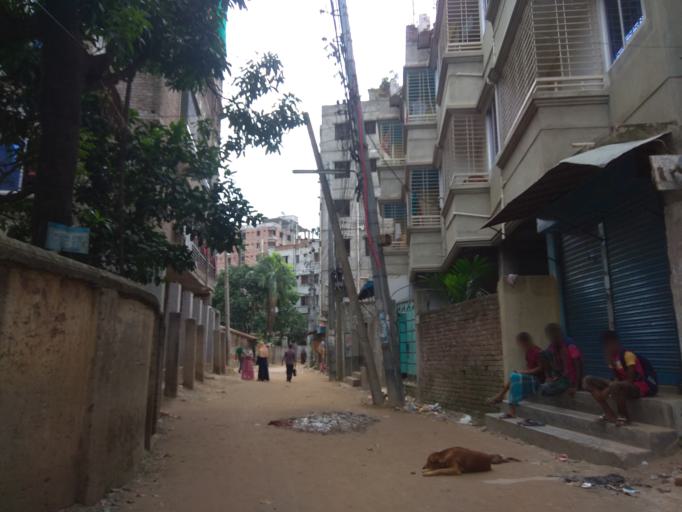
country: BD
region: Dhaka
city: Tungi
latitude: 23.8130
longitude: 90.3863
